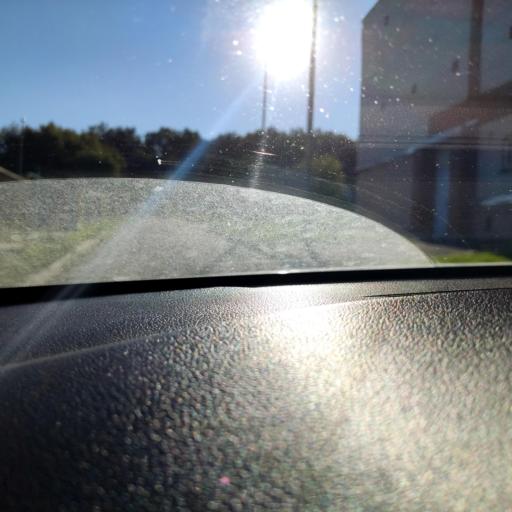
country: RU
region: Tatarstan
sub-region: Gorod Kazan'
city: Kazan
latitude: 55.8351
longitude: 49.2041
